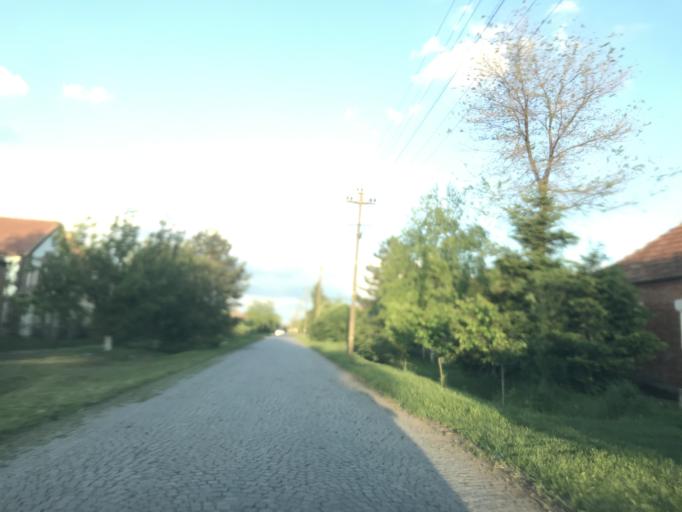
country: RS
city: Banatski Dvor
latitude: 45.5211
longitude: 20.4995
